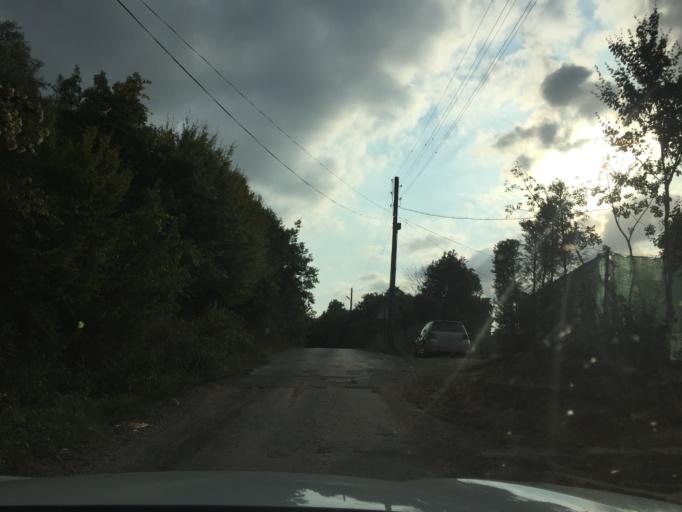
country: TR
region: Balikesir
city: Gonen
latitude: 40.0534
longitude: 27.5915
